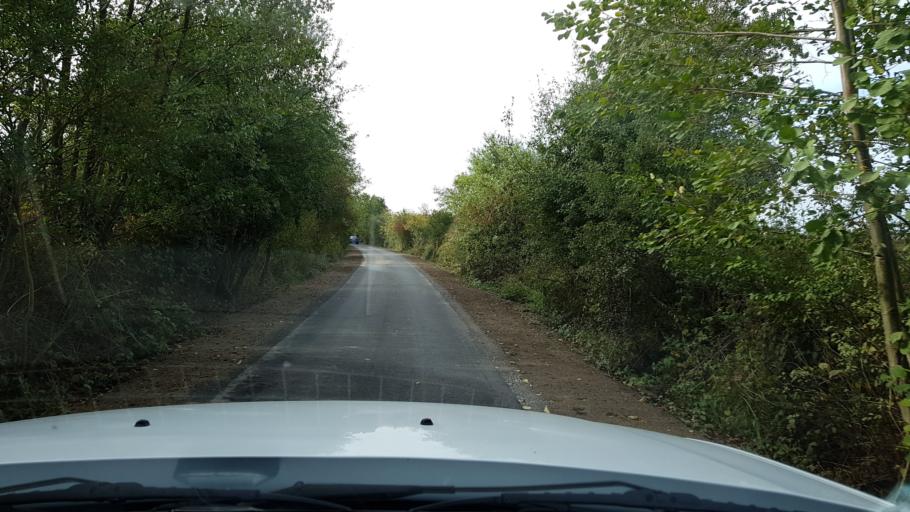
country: PL
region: West Pomeranian Voivodeship
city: Trzcinsko Zdroj
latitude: 52.9497
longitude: 14.5773
